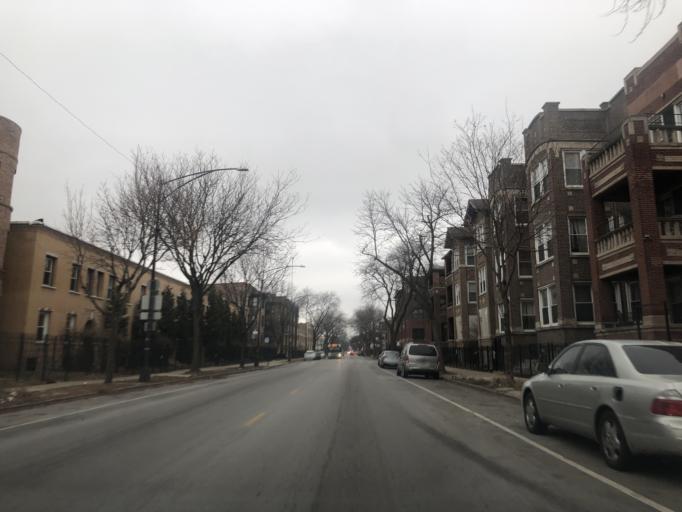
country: US
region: Illinois
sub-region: Cook County
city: Chicago
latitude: 41.7812
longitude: -87.6156
